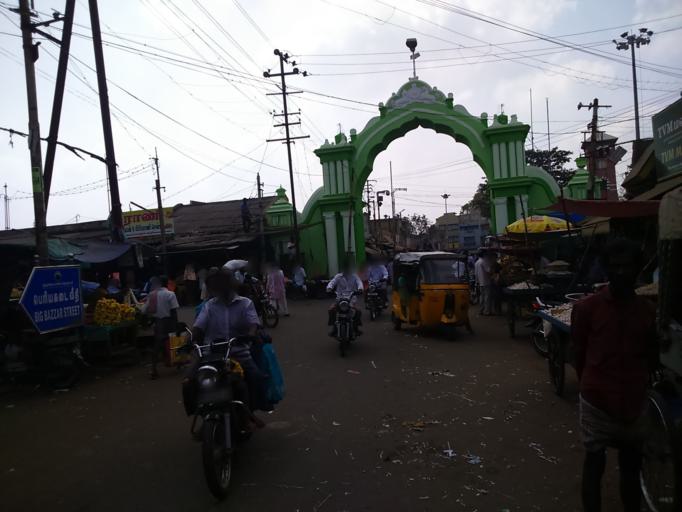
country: IN
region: Tamil Nadu
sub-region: Tiruchchirappalli
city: Tiruchirappalli
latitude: 10.8165
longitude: 78.6968
